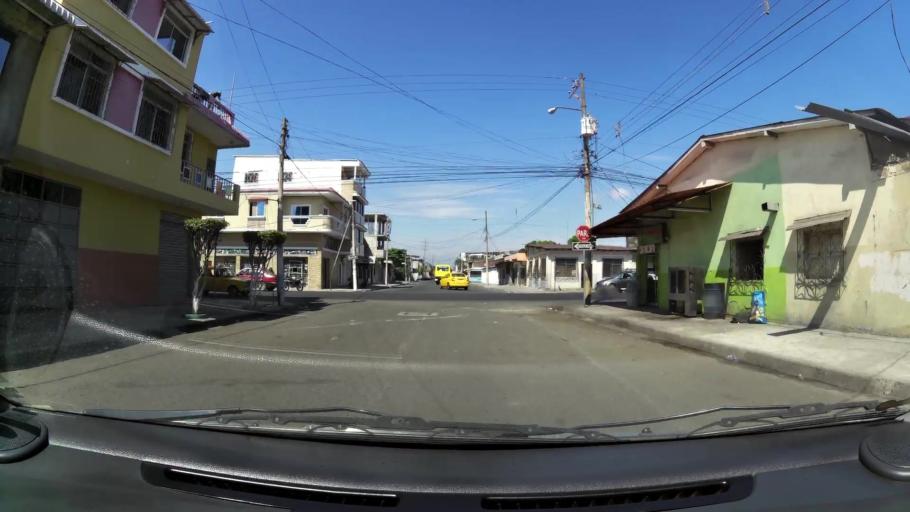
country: EC
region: Guayas
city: Guayaquil
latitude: -2.2044
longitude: -79.9347
